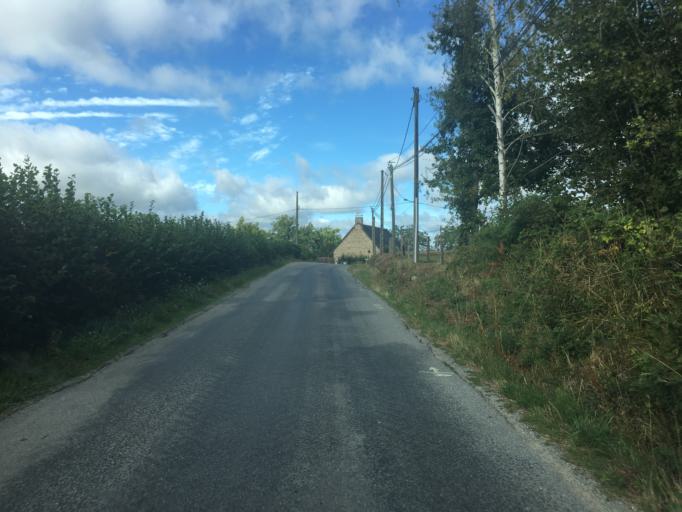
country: FR
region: Auvergne
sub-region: Departement du Cantal
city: Champagnac
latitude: 45.4148
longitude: 2.4242
